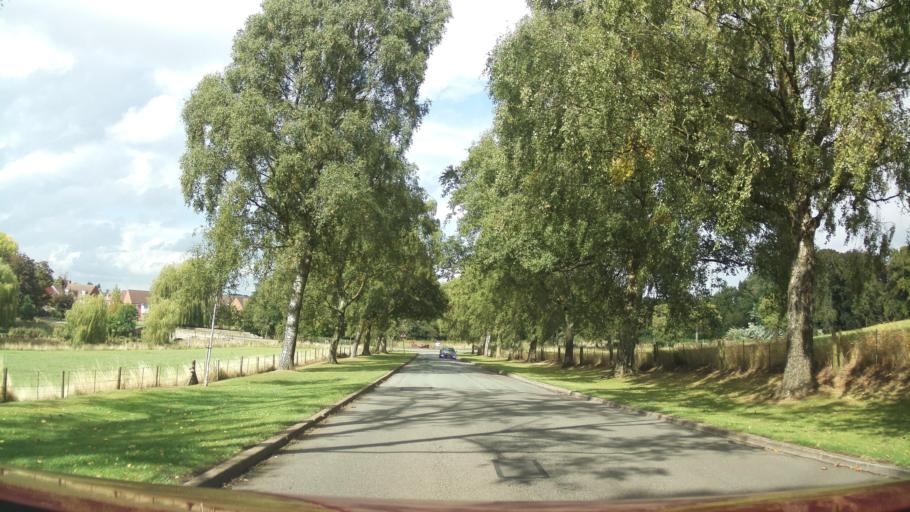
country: GB
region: England
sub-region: Staffordshire
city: Barlaston
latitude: 52.9523
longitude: -2.1611
